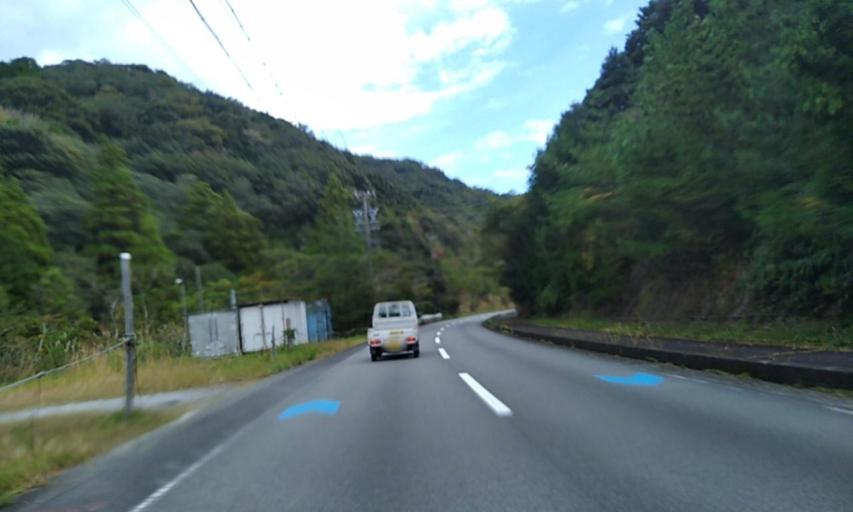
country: JP
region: Mie
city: Ise
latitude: 34.2990
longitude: 136.6122
